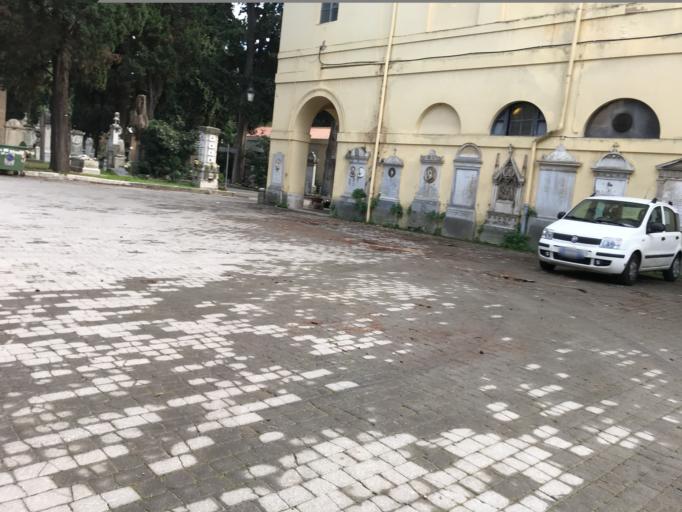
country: IT
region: Latium
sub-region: Citta metropolitana di Roma Capitale
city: Rome
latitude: 41.9023
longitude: 12.5229
